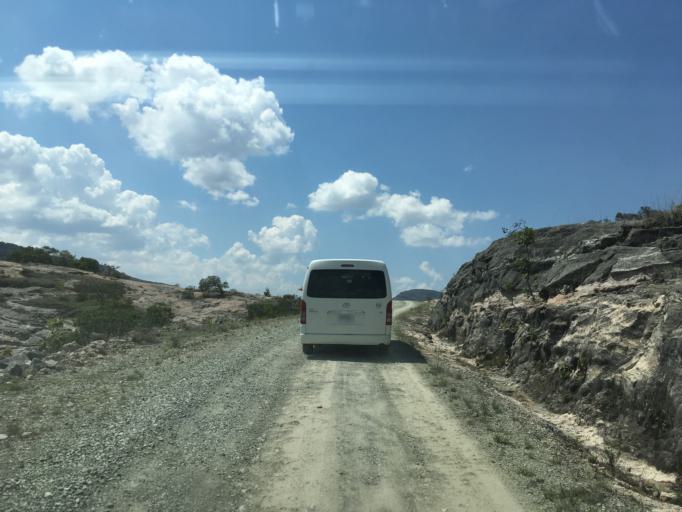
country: MX
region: Oaxaca
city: Santiago Tillo
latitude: 17.5618
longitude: -97.3380
